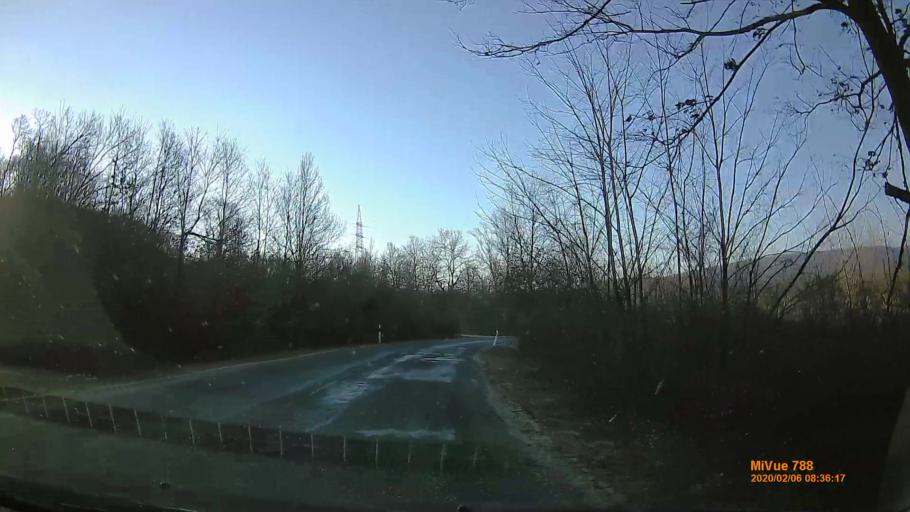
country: HU
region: Fejer
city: Szarliget
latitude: 47.5299
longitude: 18.4968
